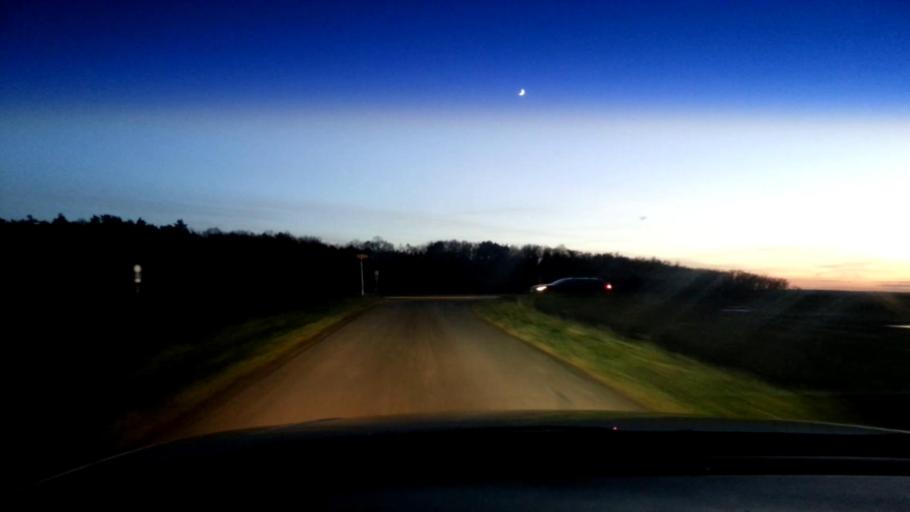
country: DE
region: Bavaria
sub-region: Upper Franconia
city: Memmelsdorf
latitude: 49.9364
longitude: 10.9875
